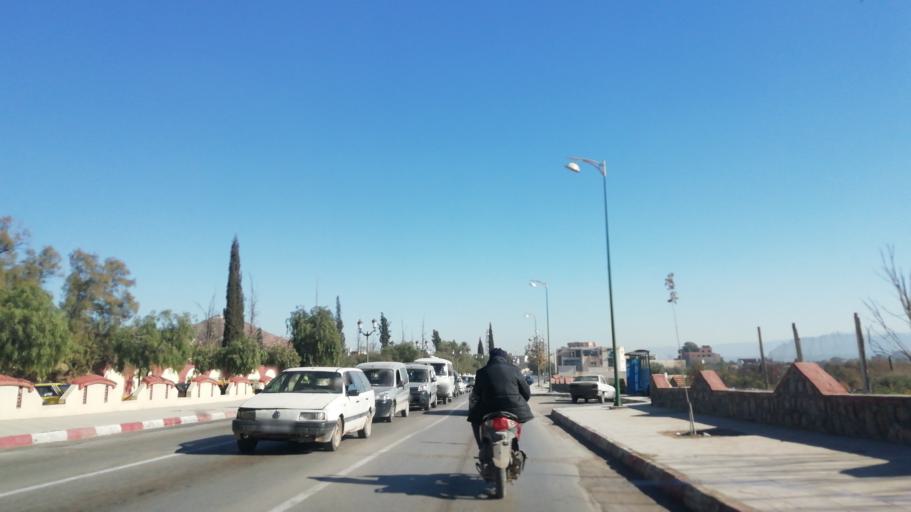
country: DZ
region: Tlemcen
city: Nedroma
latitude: 34.8460
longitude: -1.7390
